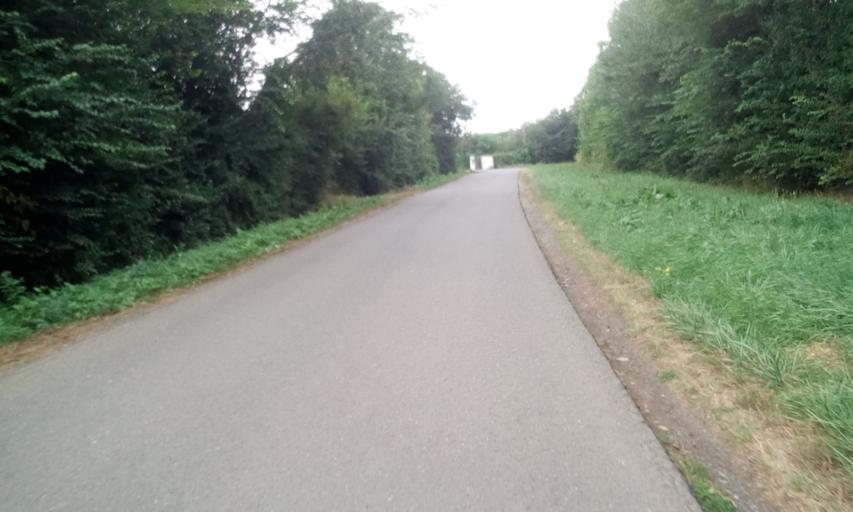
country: FR
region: Lower Normandy
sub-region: Departement du Calvados
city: Sannerville
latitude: 49.1953
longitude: -0.2234
